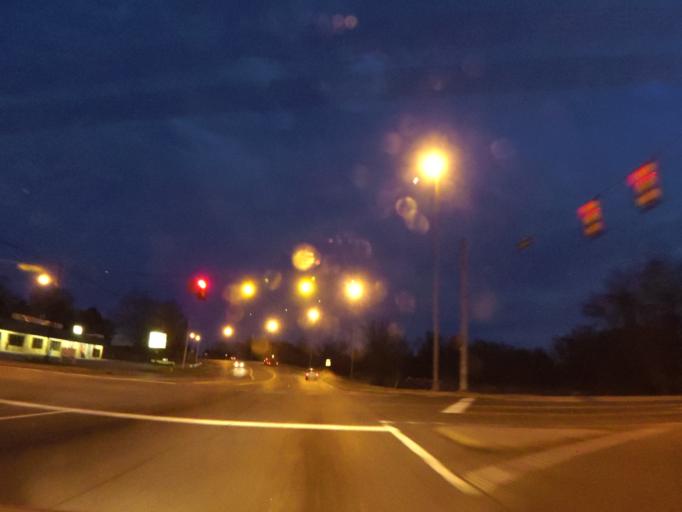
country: US
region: Tennessee
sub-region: Anderson County
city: Oak Ridge
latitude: 36.0181
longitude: -84.2848
